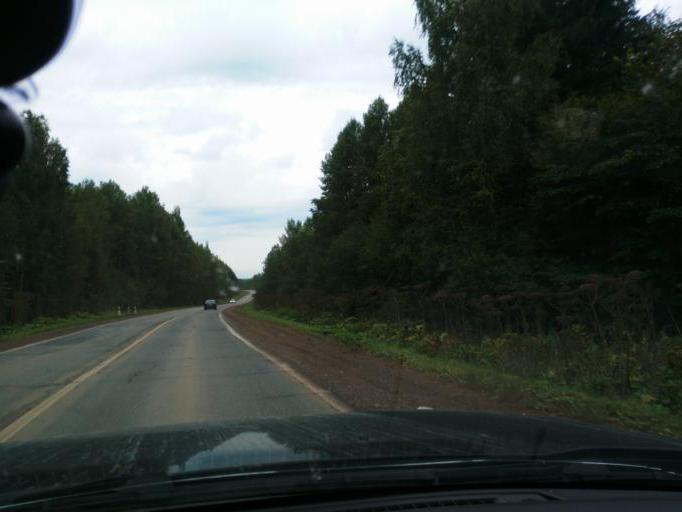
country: RU
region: Perm
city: Chernushka
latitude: 56.6781
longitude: 56.1726
